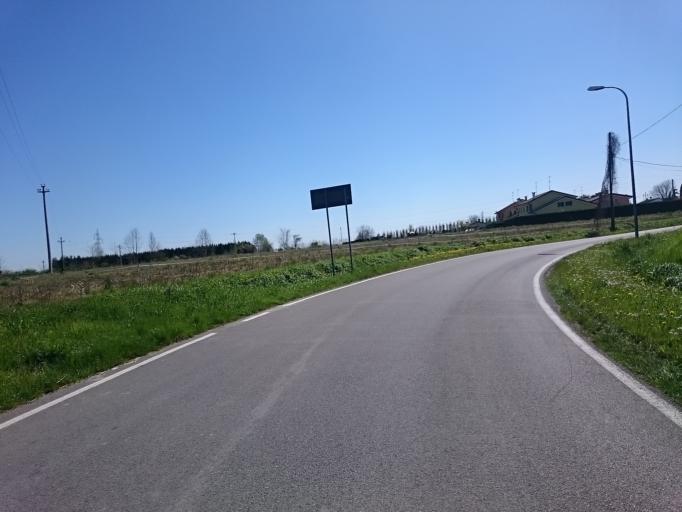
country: IT
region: Veneto
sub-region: Provincia di Padova
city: Legnaro
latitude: 45.3239
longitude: 11.9684
